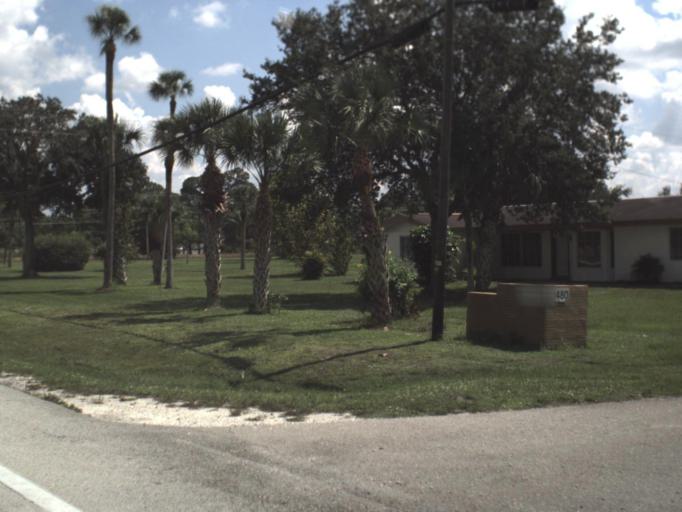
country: US
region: Florida
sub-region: Lee County
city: Fort Myers Shores
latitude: 26.7149
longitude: -81.7860
